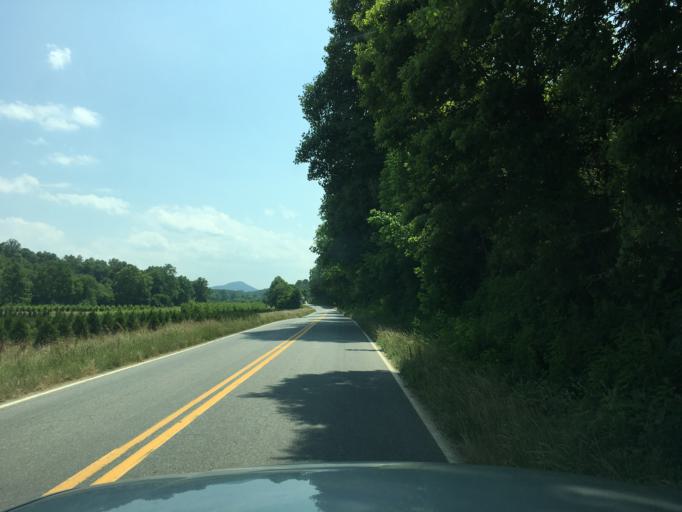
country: US
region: North Carolina
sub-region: McDowell County
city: Marion
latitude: 35.6363
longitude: -81.9579
